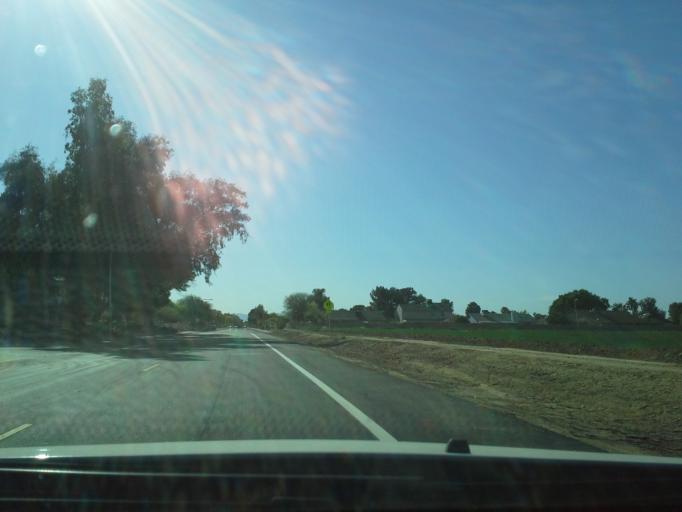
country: US
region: Arizona
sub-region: Maricopa County
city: Glendale
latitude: 33.5311
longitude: -112.2060
